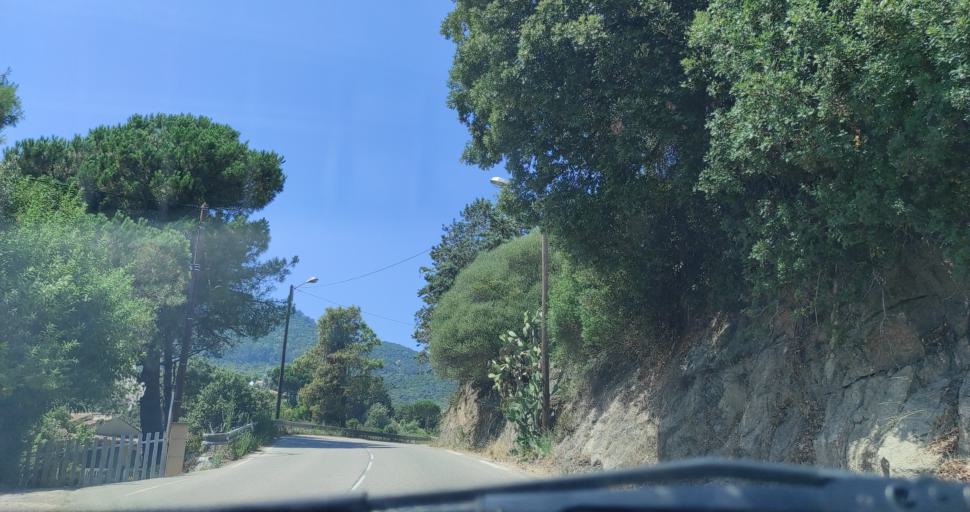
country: FR
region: Corsica
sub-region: Departement de la Corse-du-Sud
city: Ajaccio
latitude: 41.9491
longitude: 8.7343
